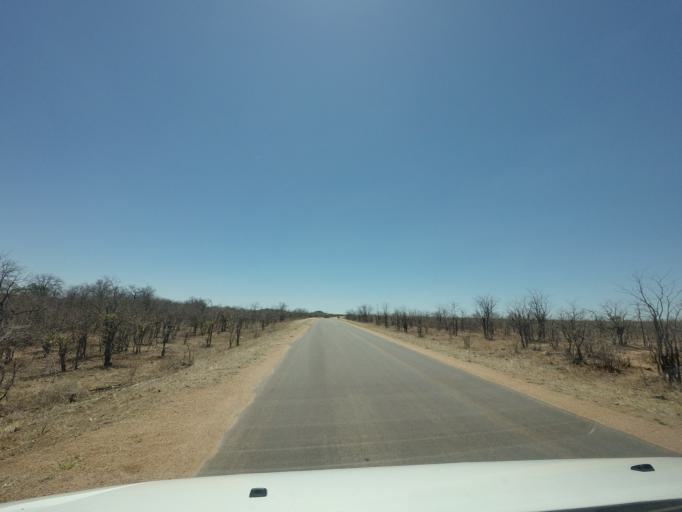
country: ZA
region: Limpopo
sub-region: Mopani District Municipality
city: Phalaborwa
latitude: -23.5382
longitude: 31.4226
